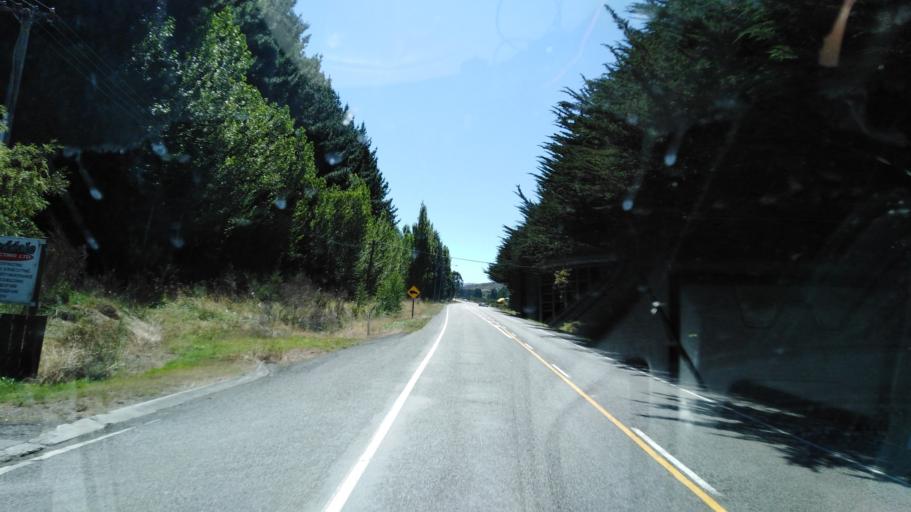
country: NZ
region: Manawatu-Wanganui
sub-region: Ruapehu District
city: Waiouru
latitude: -39.4695
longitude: 175.6706
